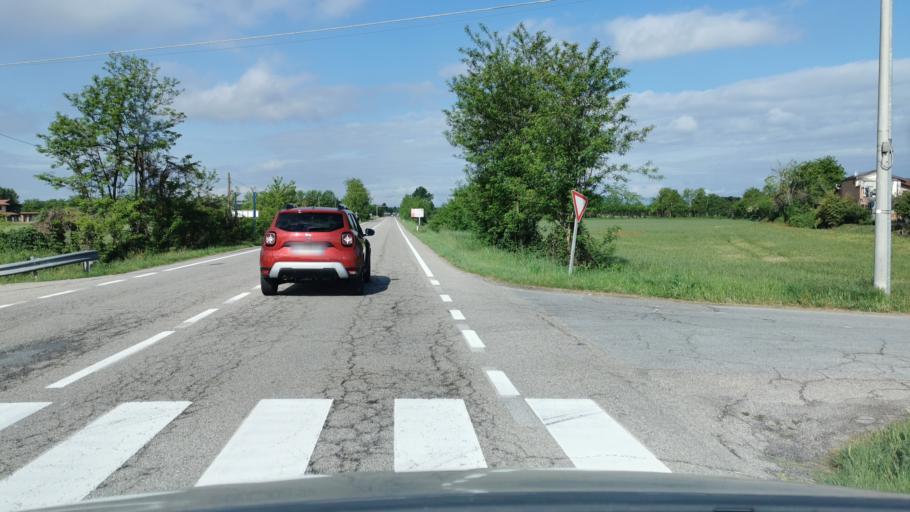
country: IT
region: Piedmont
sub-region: Provincia di Torino
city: Santena
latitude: 44.9388
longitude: 7.7727
